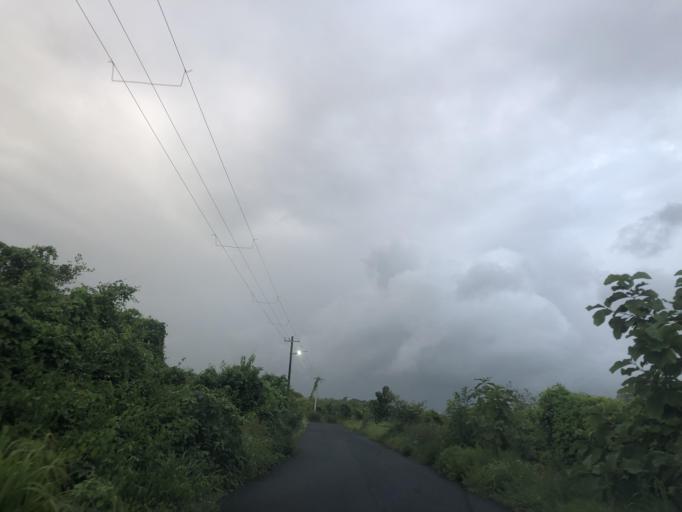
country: IN
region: Goa
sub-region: North Goa
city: Serula
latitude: 15.5112
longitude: 73.8856
